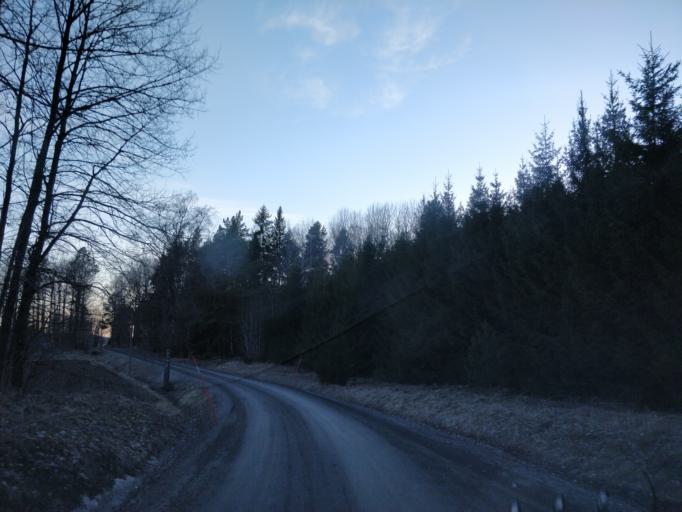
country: SE
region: Uppsala
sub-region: Enkopings Kommun
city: Orsundsbro
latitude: 59.8271
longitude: 17.1450
